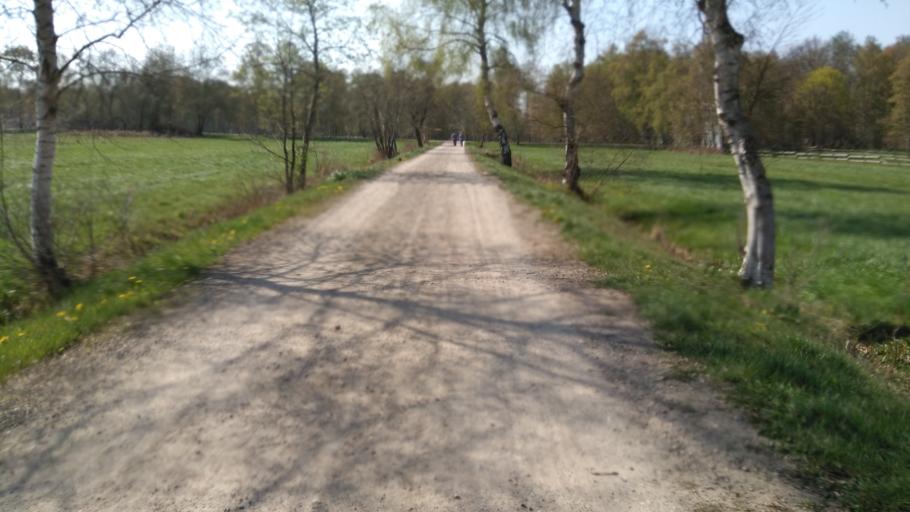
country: DE
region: Lower Saxony
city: Buxtehude
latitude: 53.4793
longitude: 9.6781
